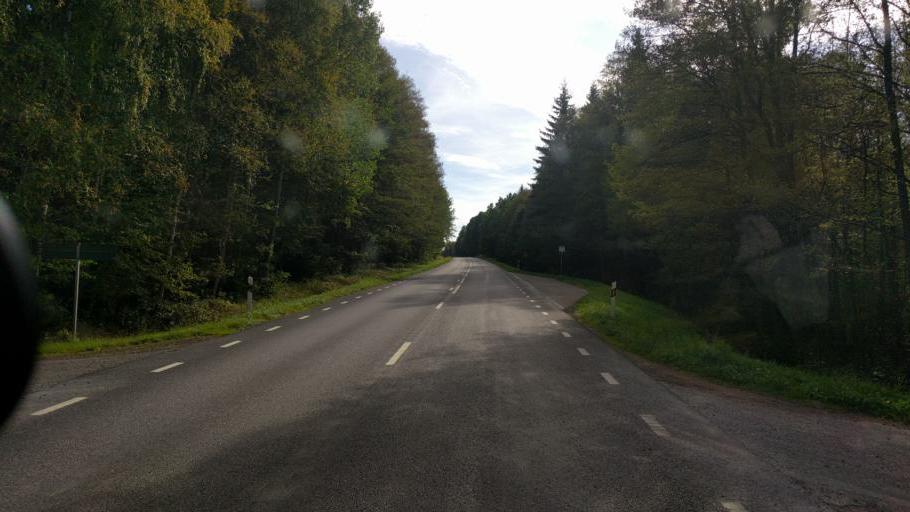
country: SE
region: OEstergoetland
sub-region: Kinda Kommun
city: Kisa
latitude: 57.9413
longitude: 15.6670
